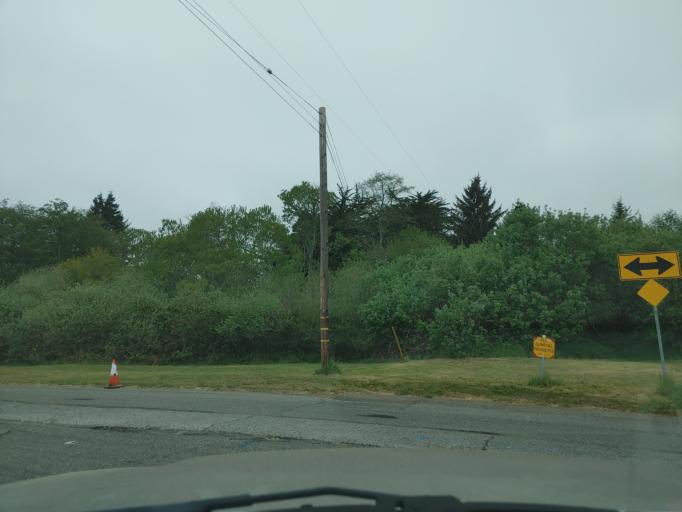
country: US
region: California
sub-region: Humboldt County
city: Bayview
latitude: 40.7757
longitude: -124.1872
